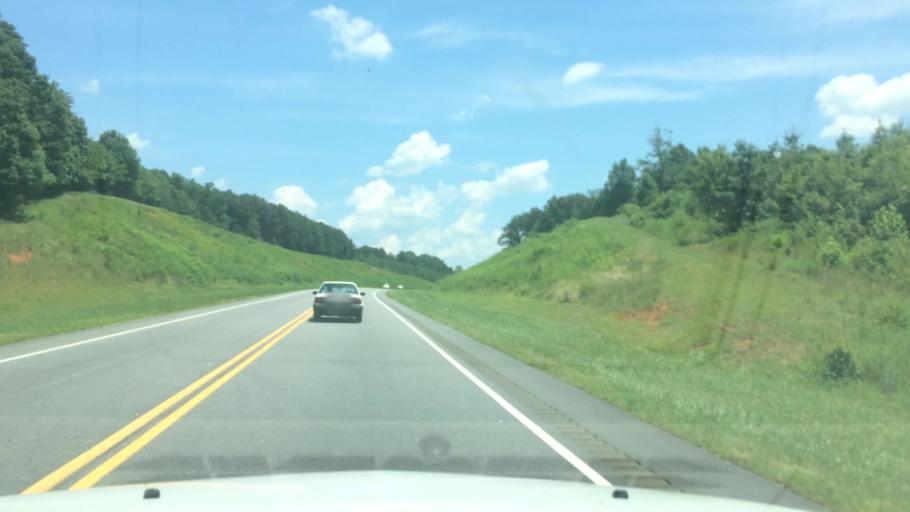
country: US
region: North Carolina
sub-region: Alexander County
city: Taylorsville
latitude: 35.9117
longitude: -81.1536
